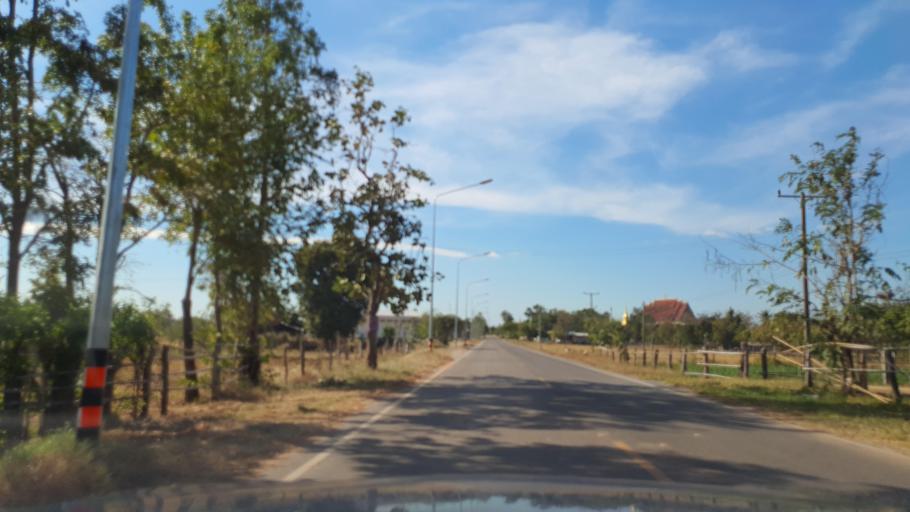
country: TH
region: Kalasin
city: Khao Wong
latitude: 16.6478
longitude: 104.1599
